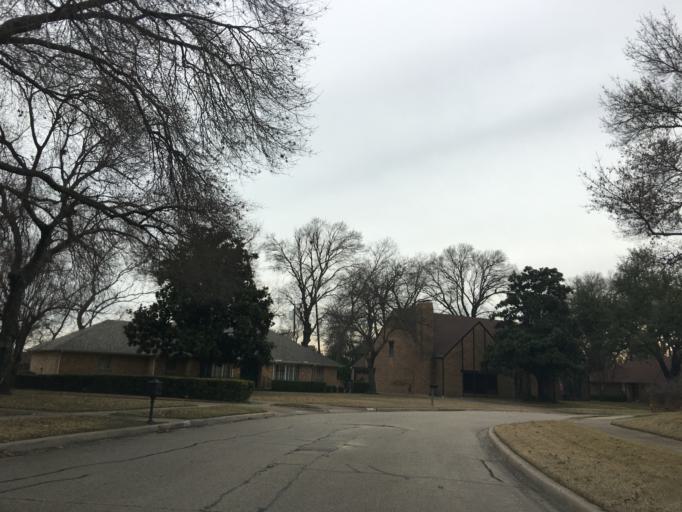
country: US
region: Texas
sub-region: Collin County
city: McKinney
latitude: 33.1969
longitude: -96.6426
